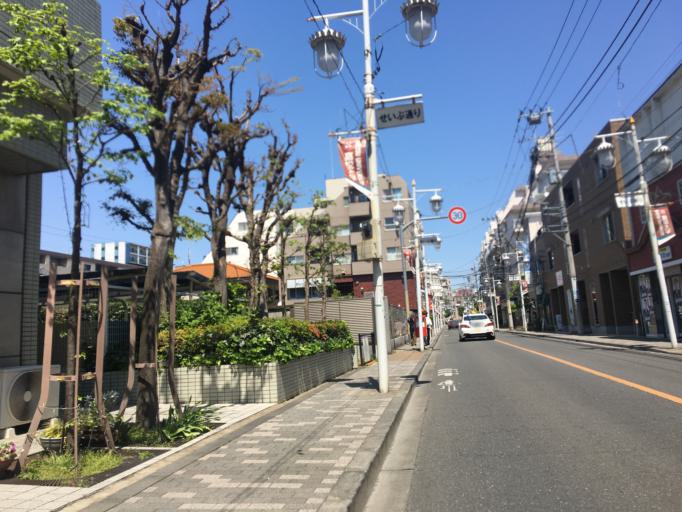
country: JP
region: Tokyo
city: Tanashicho
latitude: 35.7230
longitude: 139.5138
